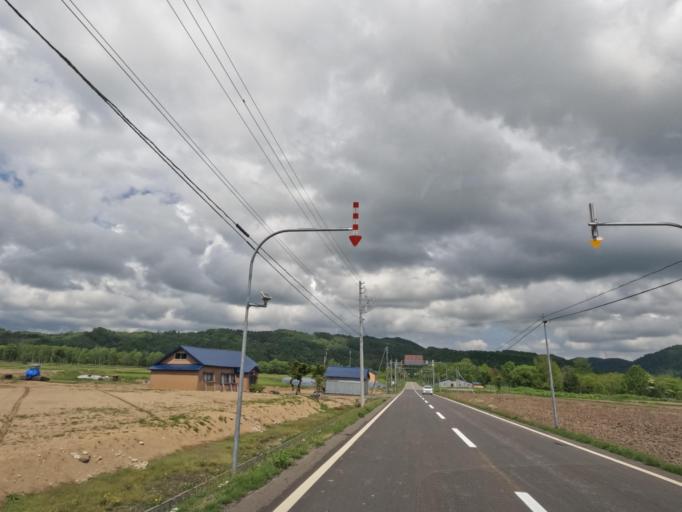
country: JP
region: Hokkaido
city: Takikawa
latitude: 43.5576
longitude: 141.6749
